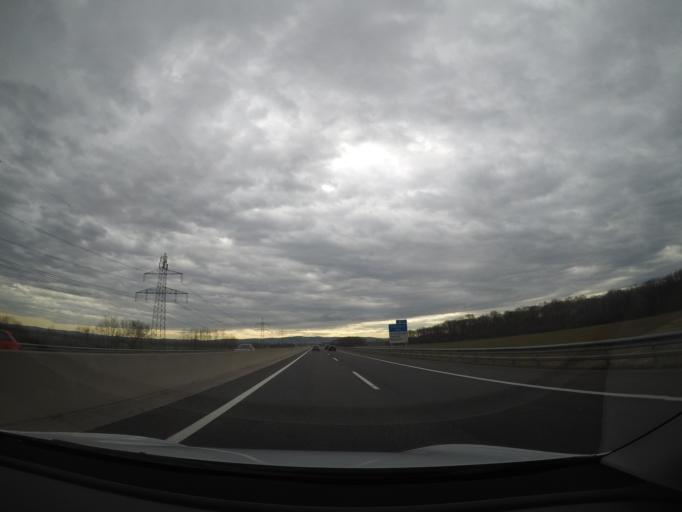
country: AT
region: Lower Austria
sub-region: Politischer Bezirk Baden
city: Ebreichsdorf
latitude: 47.9334
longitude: 16.3840
